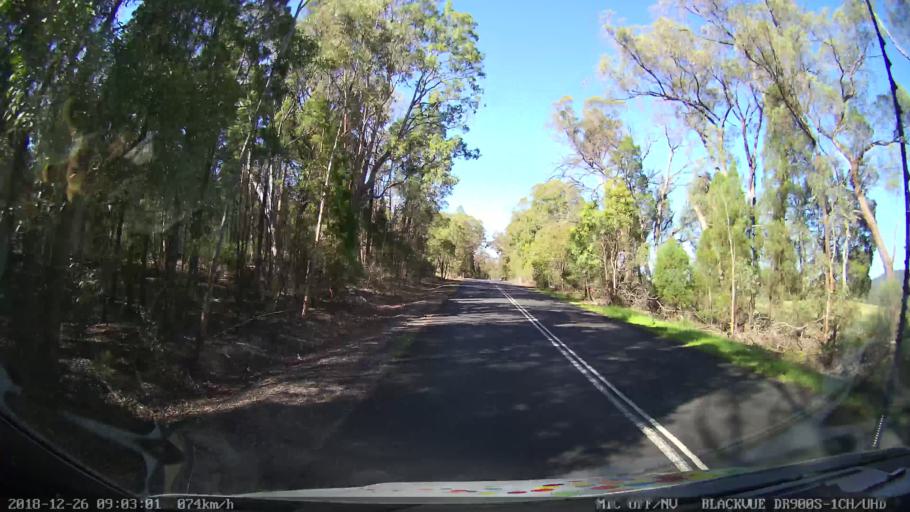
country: AU
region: New South Wales
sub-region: Mid-Western Regional
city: Kandos
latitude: -32.6584
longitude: 150.0157
